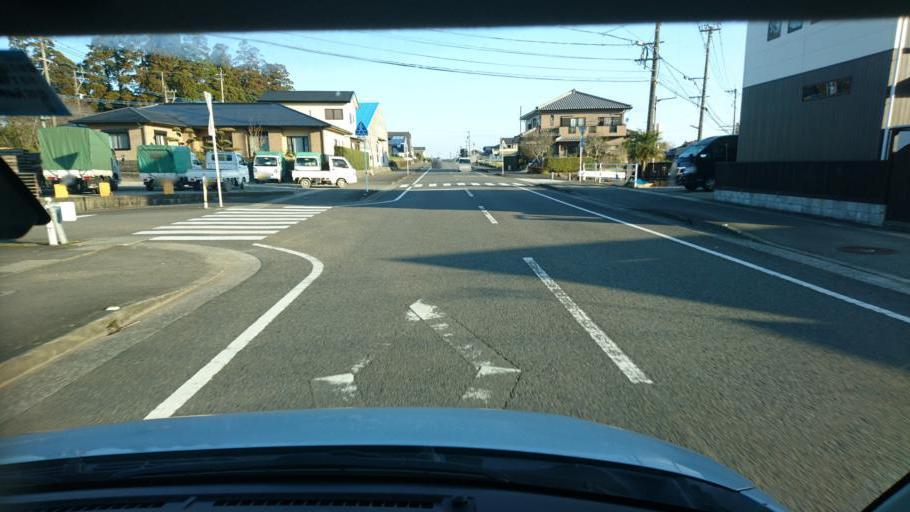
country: JP
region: Miyazaki
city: Miyazaki-shi
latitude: 31.8324
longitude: 131.4200
